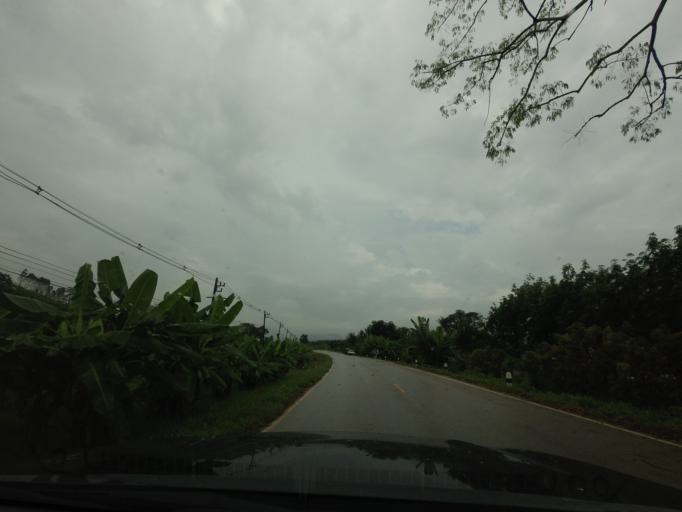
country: TH
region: Nong Khai
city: Sangkhom
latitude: 18.2126
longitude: 102.0824
